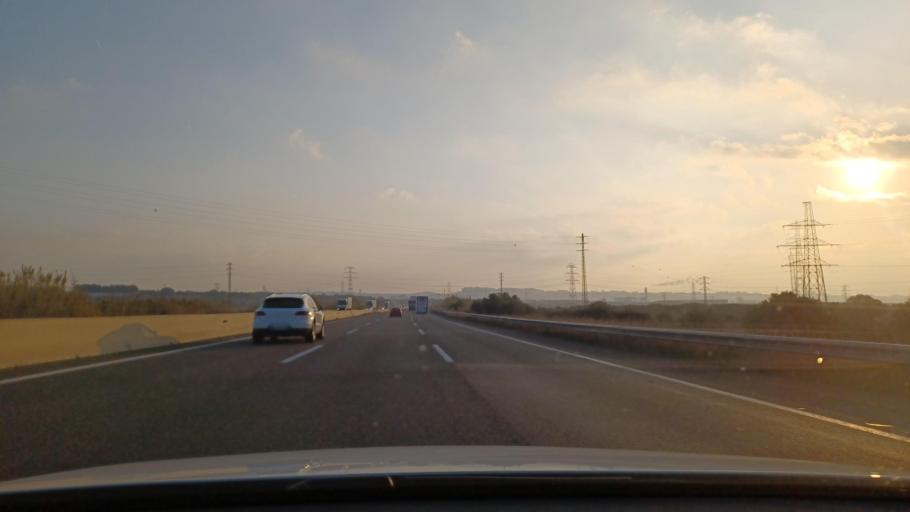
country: ES
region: Catalonia
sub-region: Provincia de Tarragona
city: Constanti
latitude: 41.1443
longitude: 1.2078
